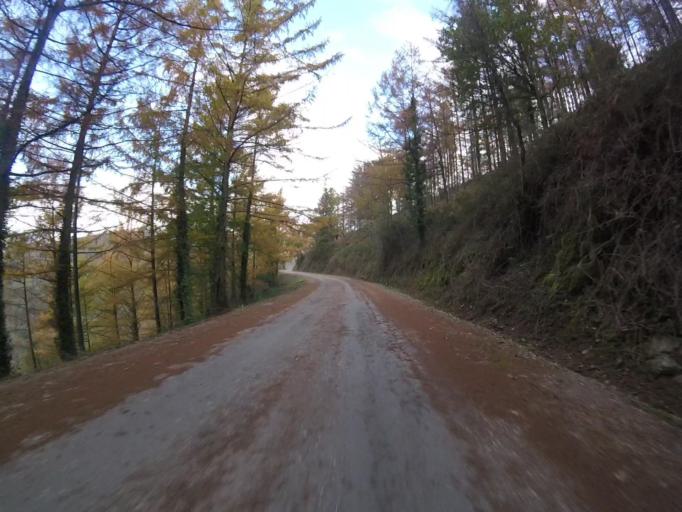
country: ES
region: Navarre
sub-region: Provincia de Navarra
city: Goizueta
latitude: 43.2163
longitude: -1.8516
